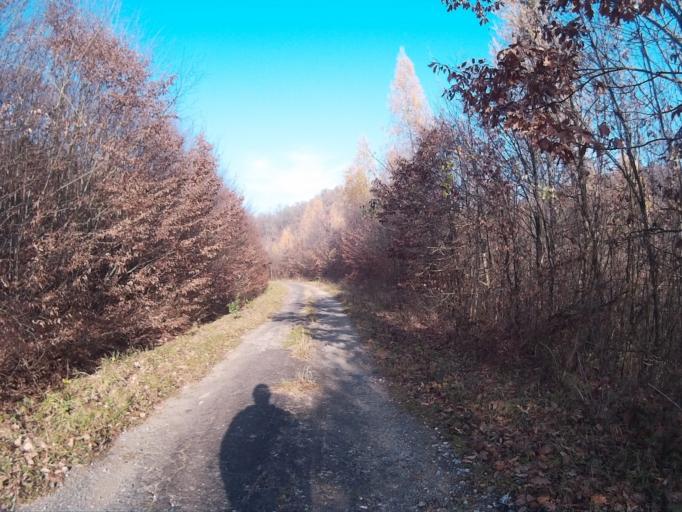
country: HU
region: Heves
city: Felsotarkany
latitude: 47.9981
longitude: 20.3921
